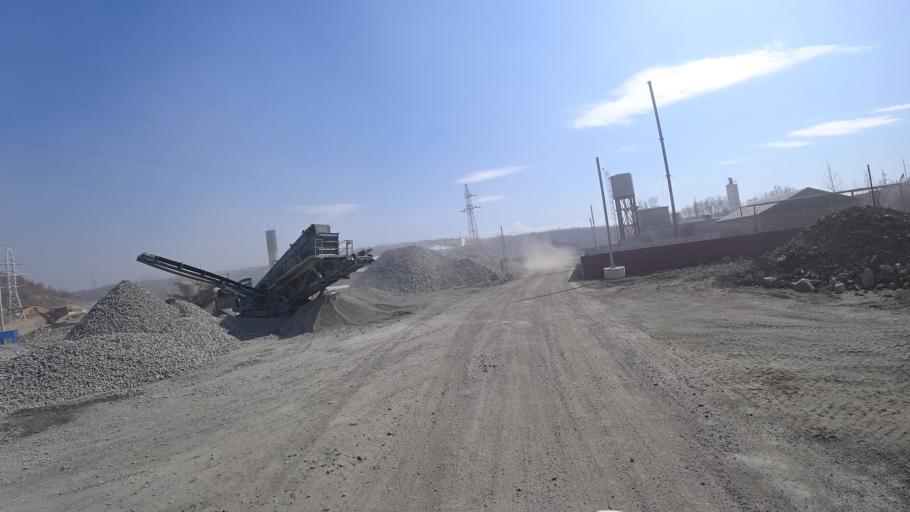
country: RU
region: Amur
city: Novobureyskiy
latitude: 49.7914
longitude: 129.9621
